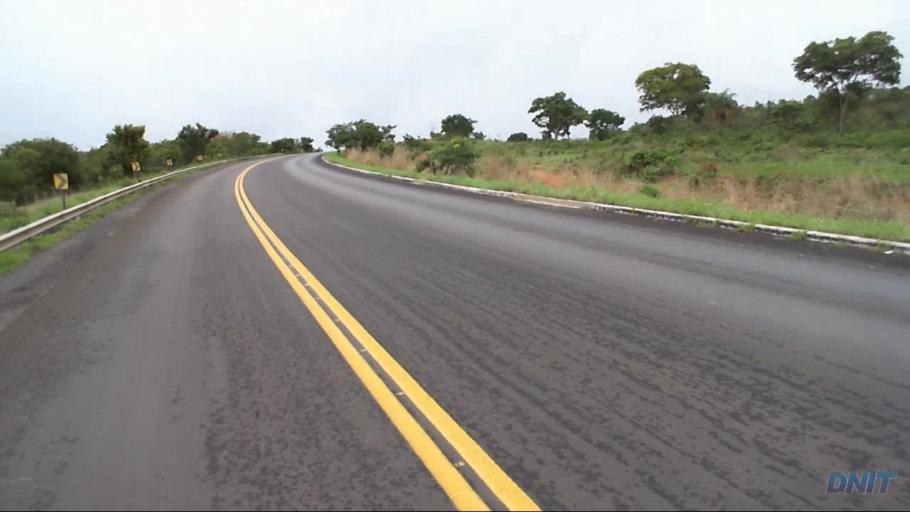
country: BR
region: Goias
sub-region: Padre Bernardo
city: Padre Bernardo
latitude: -15.1938
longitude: -48.4390
